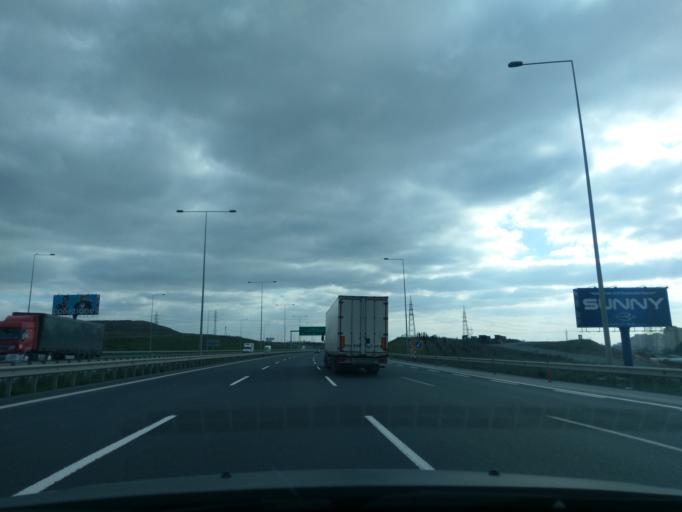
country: TR
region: Istanbul
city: Basaksehir
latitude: 41.1236
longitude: 28.8116
